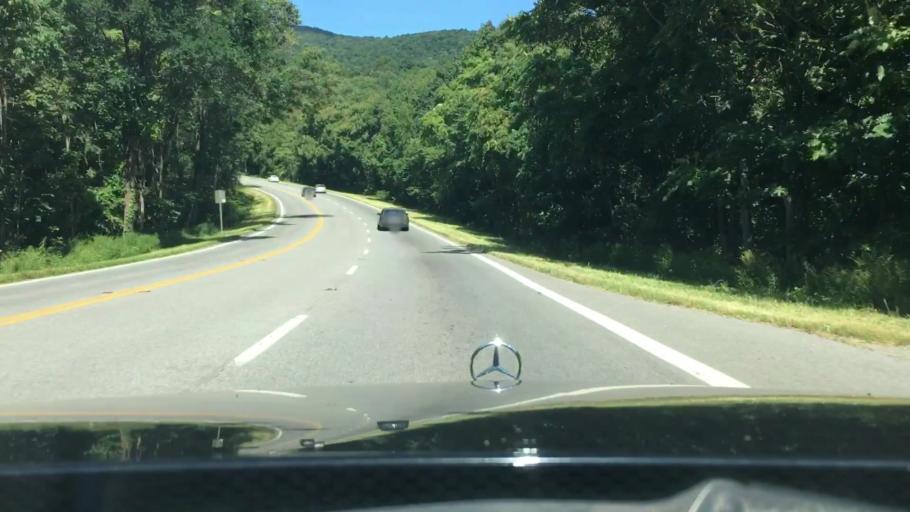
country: US
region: Virginia
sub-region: City of Waynesboro
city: Waynesboro
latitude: 38.0357
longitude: -78.8130
